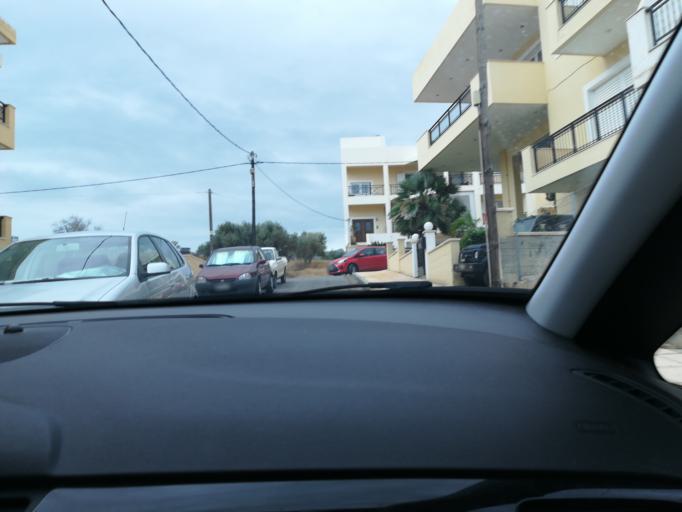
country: GR
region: Crete
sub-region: Nomos Lasithiou
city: Siteia
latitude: 35.2033
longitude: 26.0990
